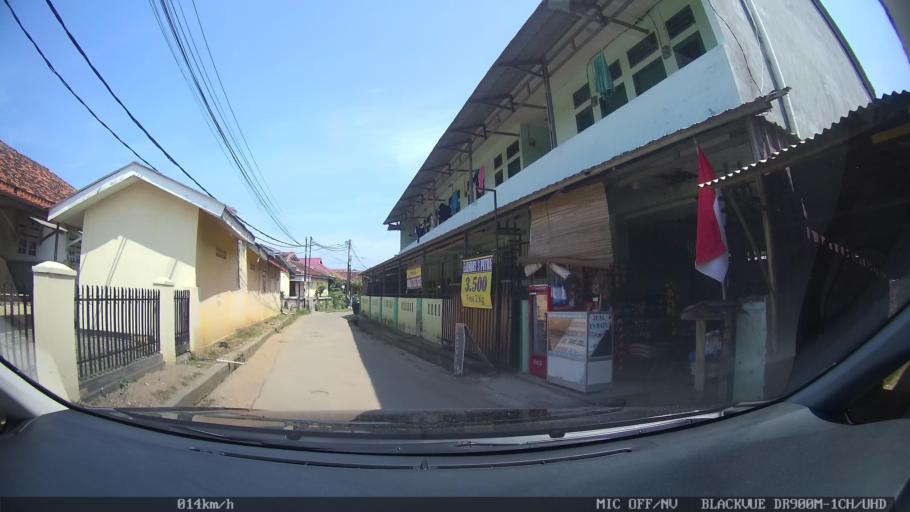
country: ID
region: Lampung
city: Kedaton
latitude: -5.3656
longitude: 105.2488
